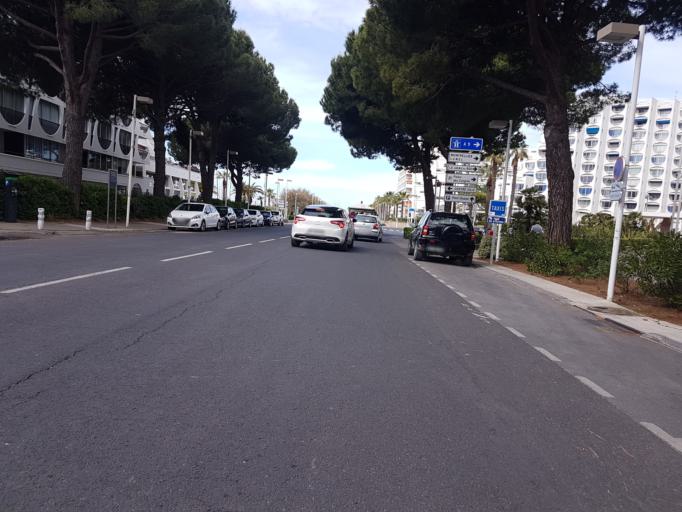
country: FR
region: Languedoc-Roussillon
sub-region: Departement de l'Herault
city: La Grande-Motte
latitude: 43.5613
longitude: 4.0832
